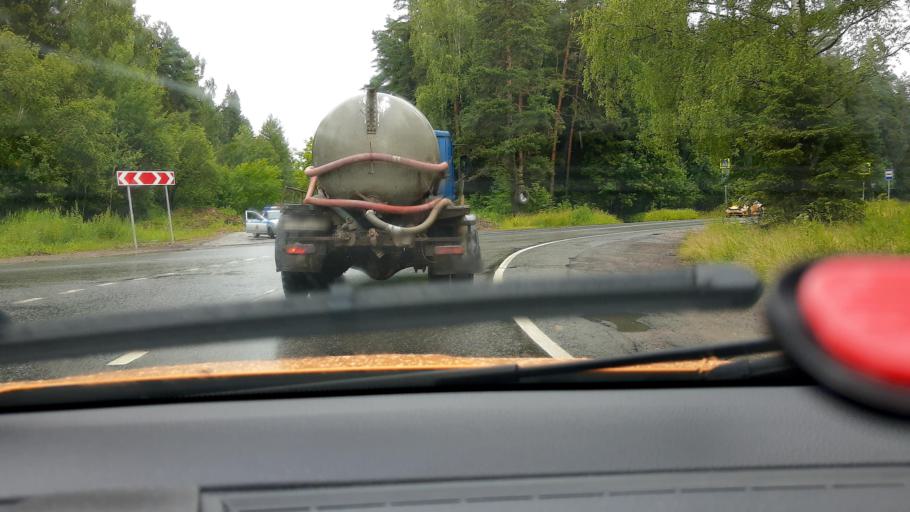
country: RU
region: Moskovskaya
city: Pirogovskiy
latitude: 56.0001
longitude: 37.6815
